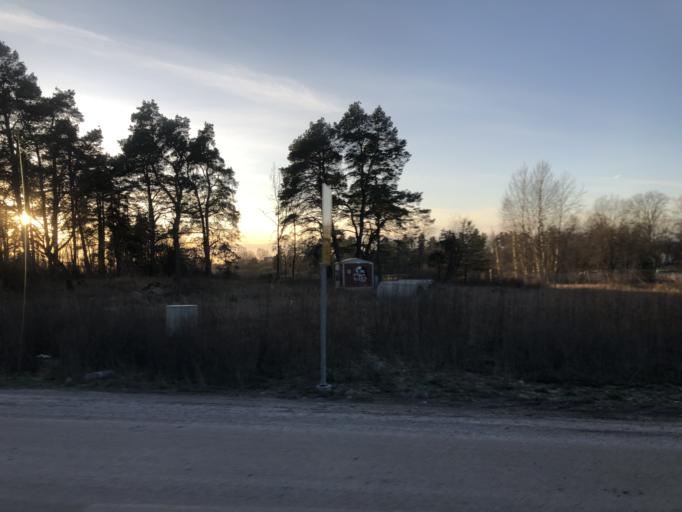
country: SE
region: Stockholm
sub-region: Jarfalla Kommun
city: Jakobsberg
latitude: 59.4101
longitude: 17.8850
